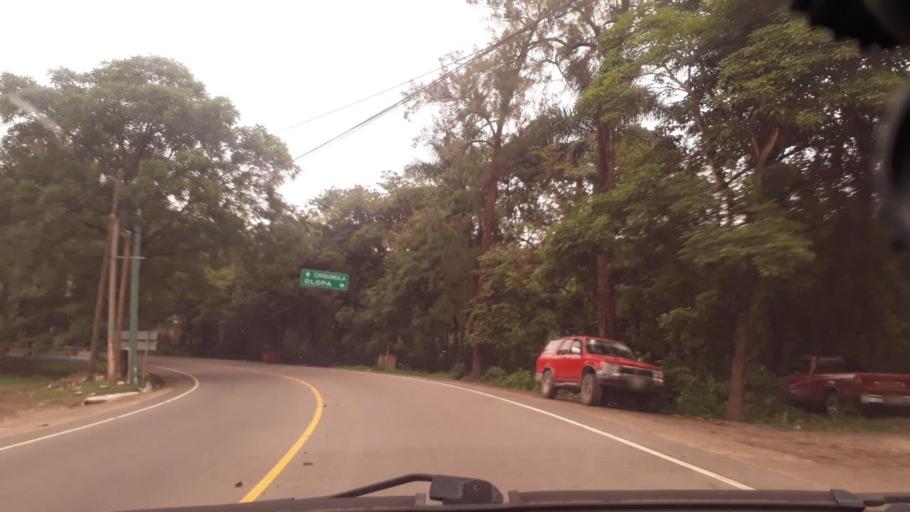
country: GT
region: Chiquimula
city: Quezaltepeque
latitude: 14.6364
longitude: -89.4466
